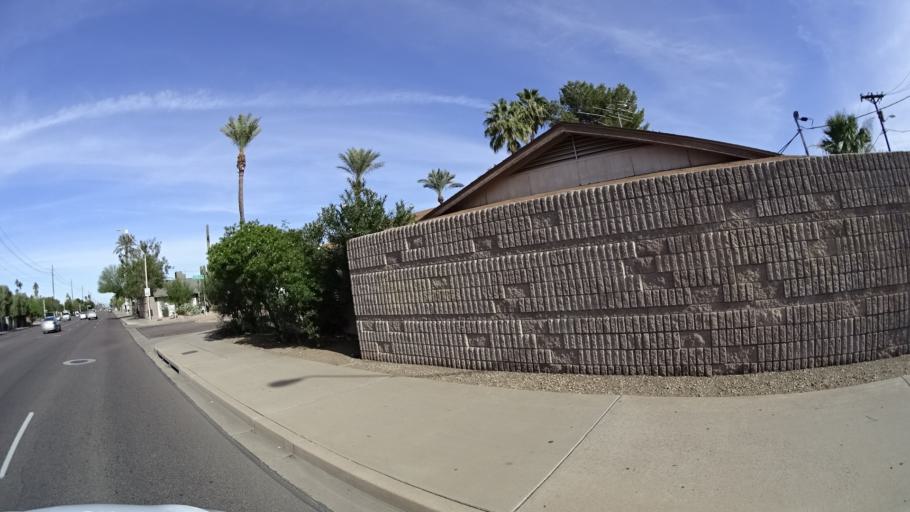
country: US
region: Arizona
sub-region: Maricopa County
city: Tempe Junction
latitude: 33.3965
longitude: -111.9262
